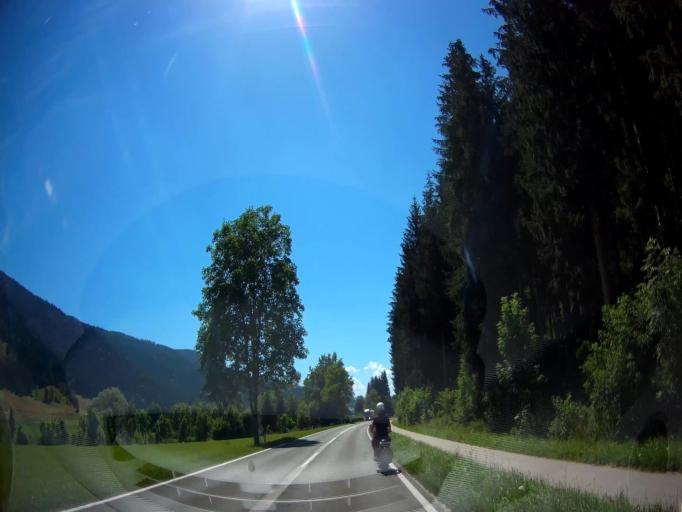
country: AT
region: Carinthia
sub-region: Politischer Bezirk Sankt Veit an der Glan
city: Gurk
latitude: 46.8696
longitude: 14.2741
